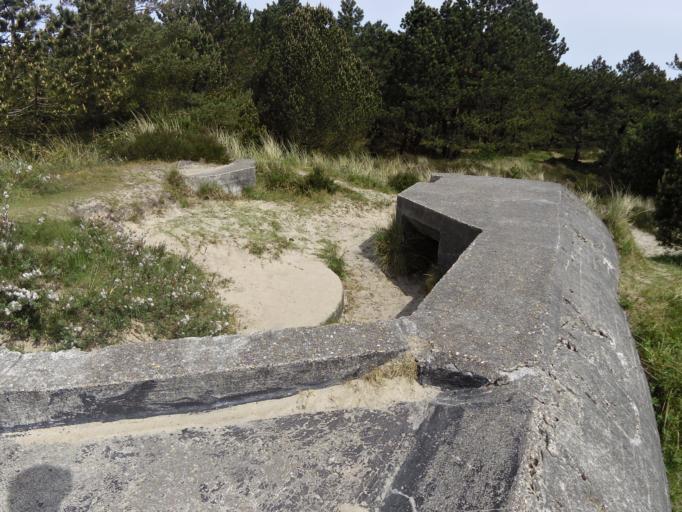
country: DE
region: Schleswig-Holstein
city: List
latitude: 55.1513
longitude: 8.5315
